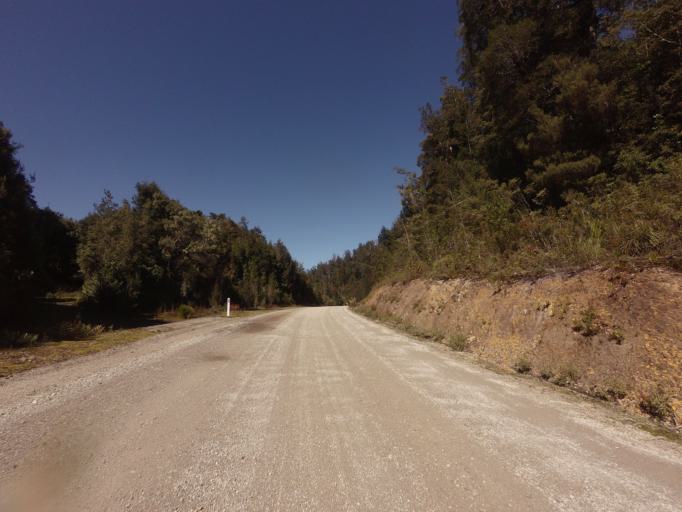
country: AU
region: Tasmania
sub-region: Huon Valley
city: Geeveston
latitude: -42.8392
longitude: 146.3769
